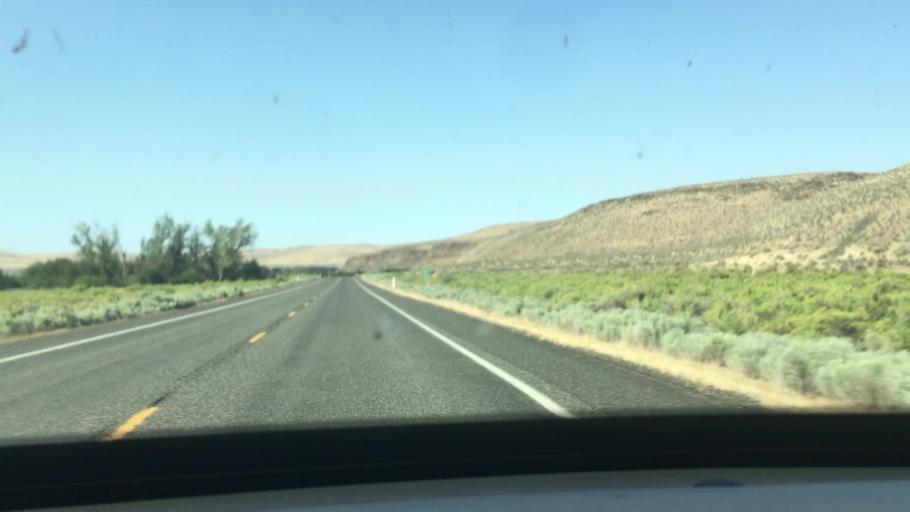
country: US
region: Washington
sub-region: Yakima County
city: Toppenish
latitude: 46.2277
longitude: -120.4250
